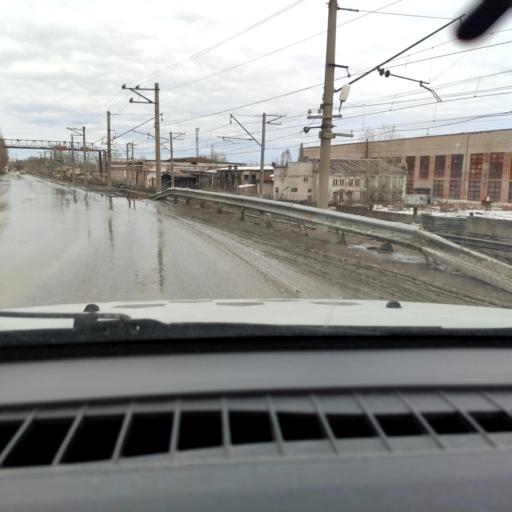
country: RU
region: Perm
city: Perm
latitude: 58.1042
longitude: 56.3154
